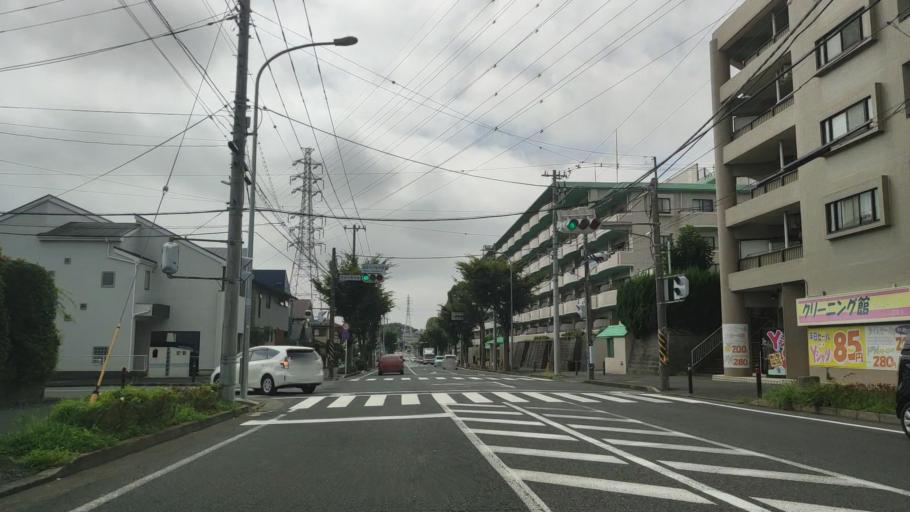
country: JP
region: Kanagawa
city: Fujisawa
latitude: 35.4159
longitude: 139.5227
